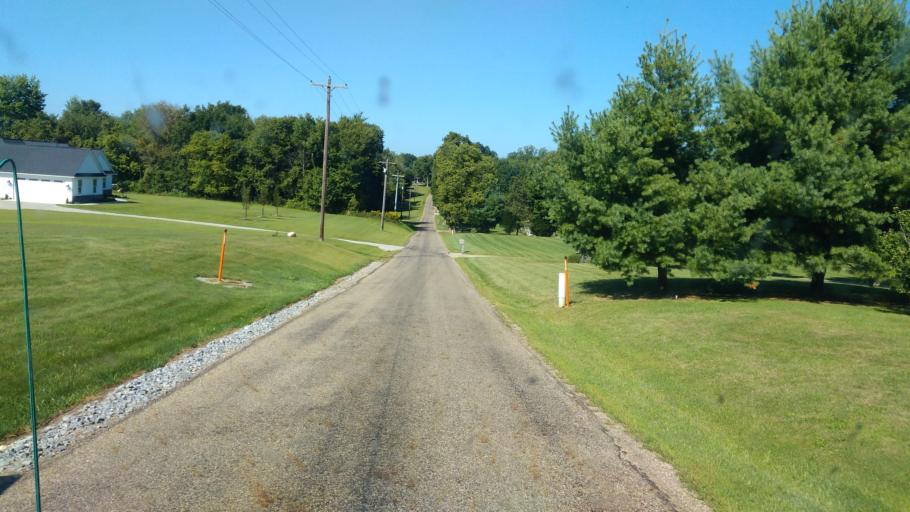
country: US
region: Ohio
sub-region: Knox County
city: Mount Vernon
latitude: 40.4548
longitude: -82.4808
